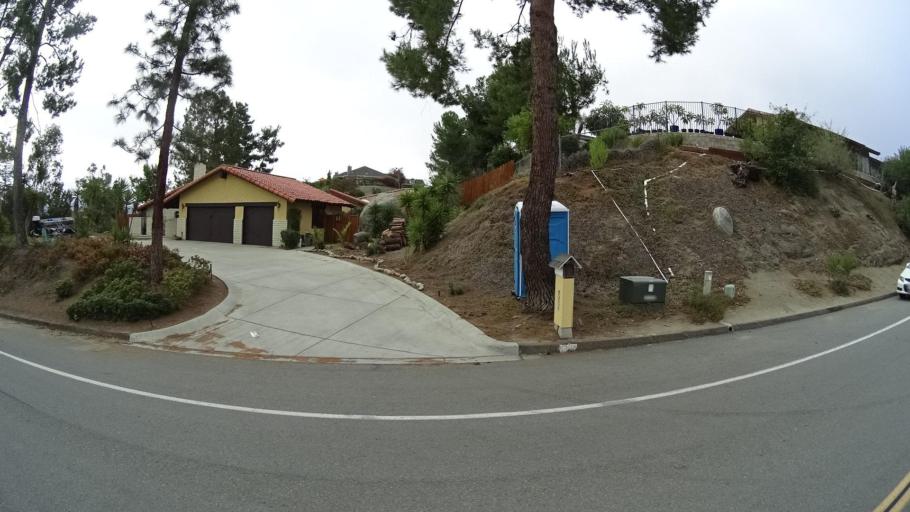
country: US
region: California
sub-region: San Diego County
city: Granite Hills
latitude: 32.7745
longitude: -116.9138
